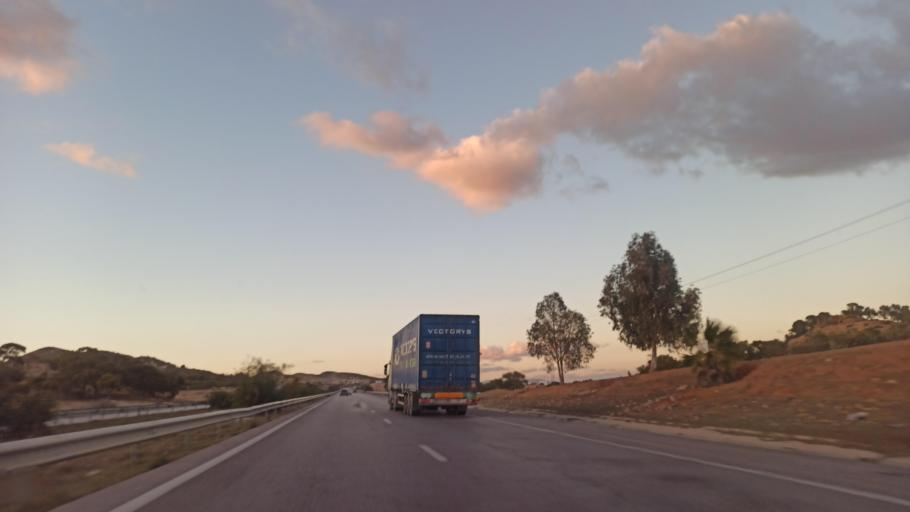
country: TN
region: Susah
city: Harqalah
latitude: 36.2224
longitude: 10.4168
